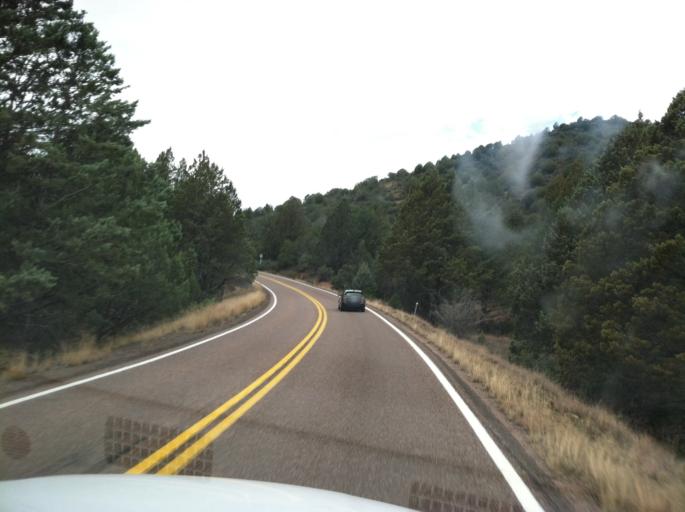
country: US
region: Arizona
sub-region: Gila County
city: Pine
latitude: 34.3186
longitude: -111.3802
